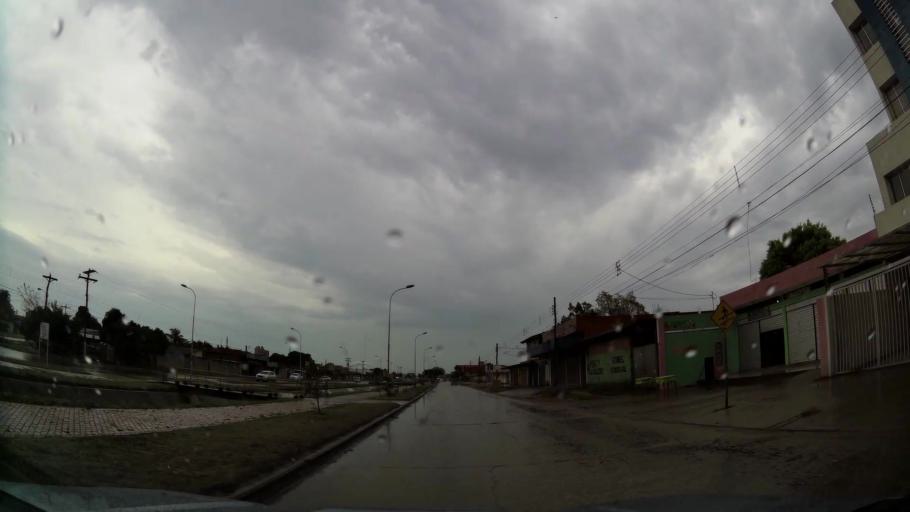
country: BO
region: Santa Cruz
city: Santa Cruz de la Sierra
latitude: -17.8118
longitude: -63.1388
